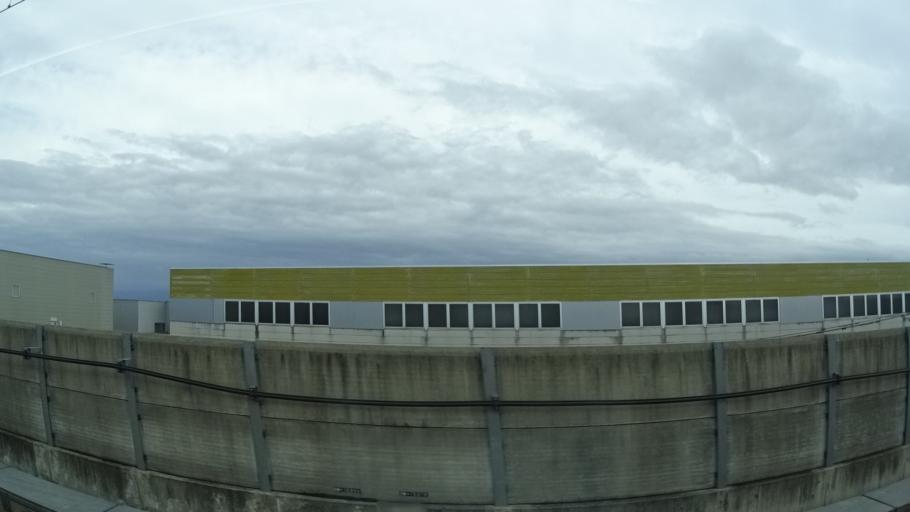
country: JP
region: Toyama
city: Toyama-shi
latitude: 36.7034
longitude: 137.2355
